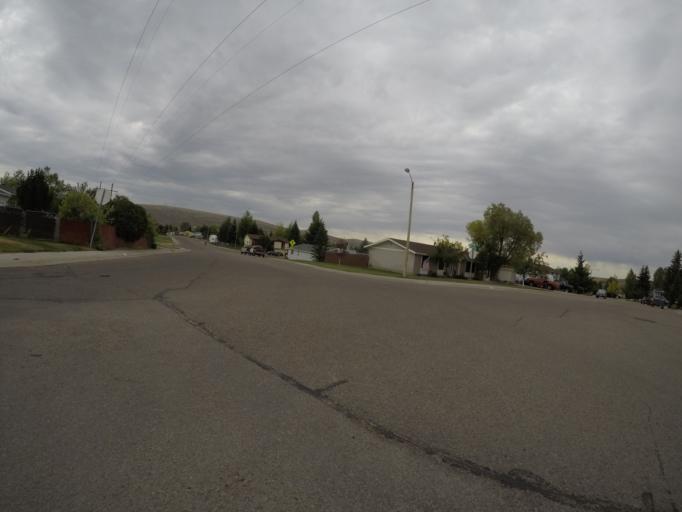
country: US
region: Wyoming
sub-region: Lincoln County
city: Kemmerer
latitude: 41.7906
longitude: -110.5514
